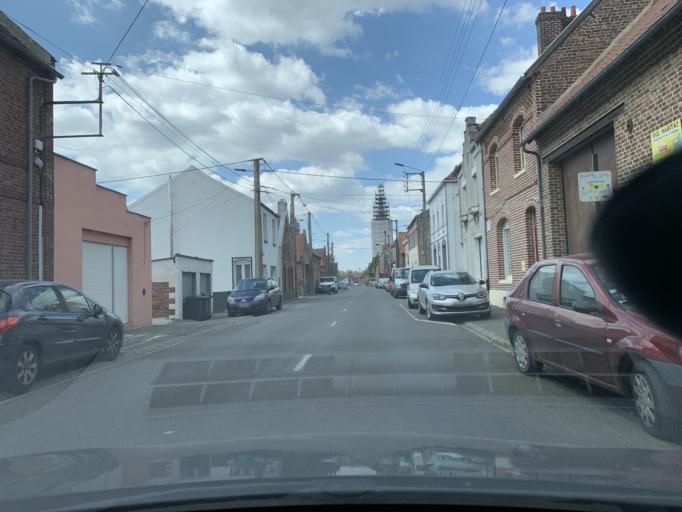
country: FR
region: Nord-Pas-de-Calais
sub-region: Departement du Pas-de-Calais
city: Ecourt-Saint-Quentin
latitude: 50.2510
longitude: 3.0729
